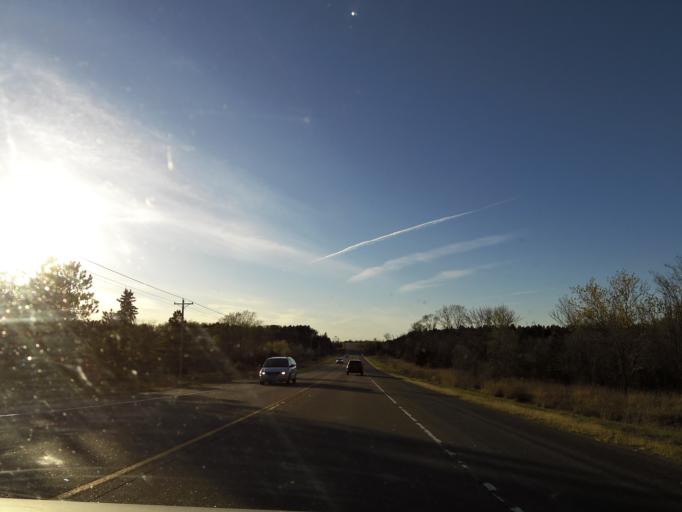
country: US
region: Wisconsin
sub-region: Pierce County
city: Prescott
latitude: 44.6964
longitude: -92.8214
